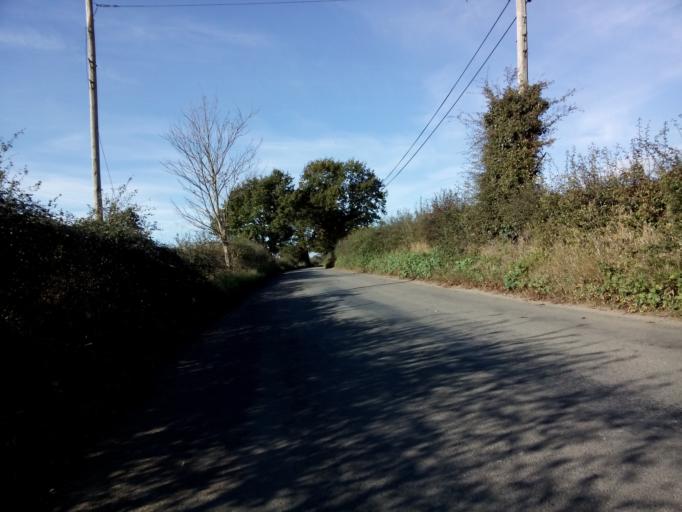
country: GB
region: England
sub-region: Suffolk
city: Bramford
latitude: 52.0255
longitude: 1.1019
